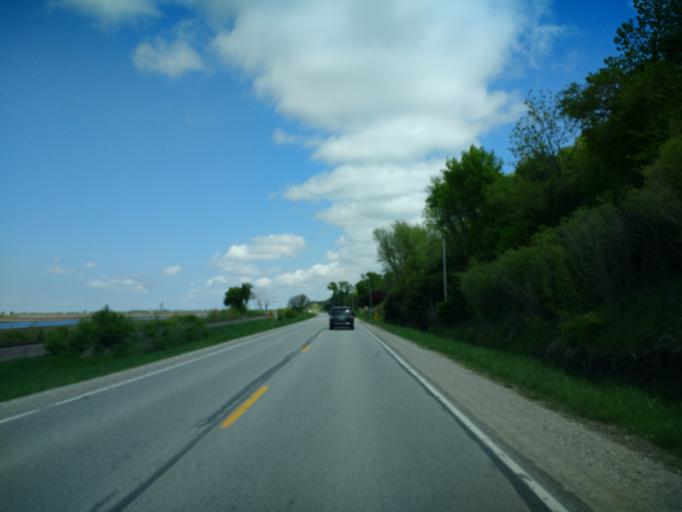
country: US
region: Iowa
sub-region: Harrison County
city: Missouri Valley
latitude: 41.4448
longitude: -95.8708
